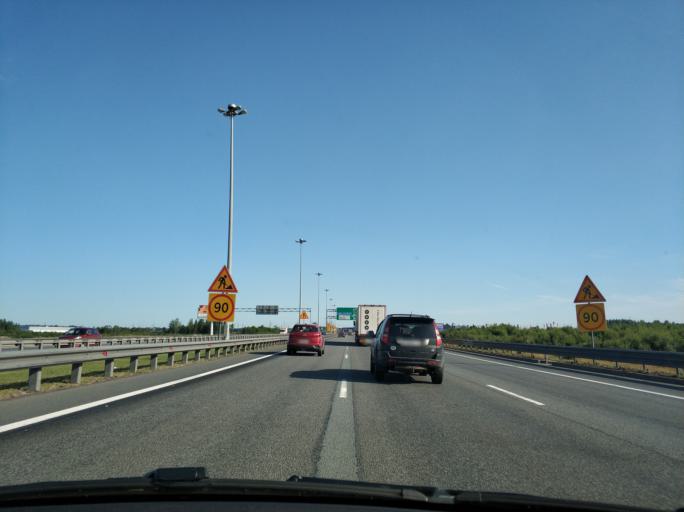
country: RU
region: Leningrad
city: Bugry
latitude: 60.0792
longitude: 30.3802
